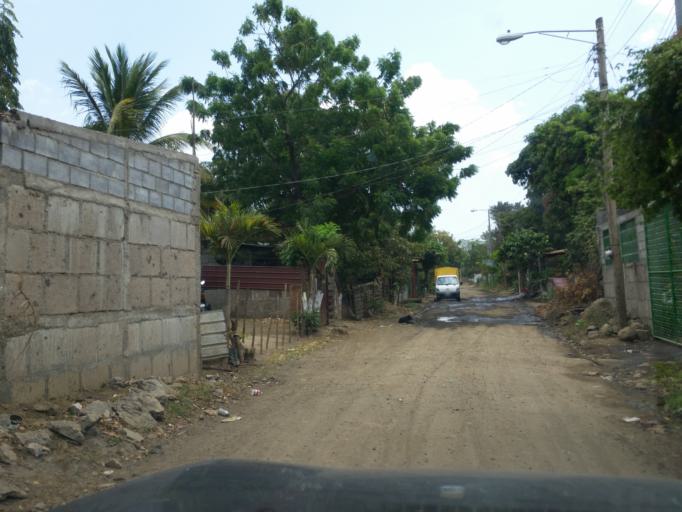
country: NI
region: Managua
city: Managua
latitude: 12.1217
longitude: -86.1647
